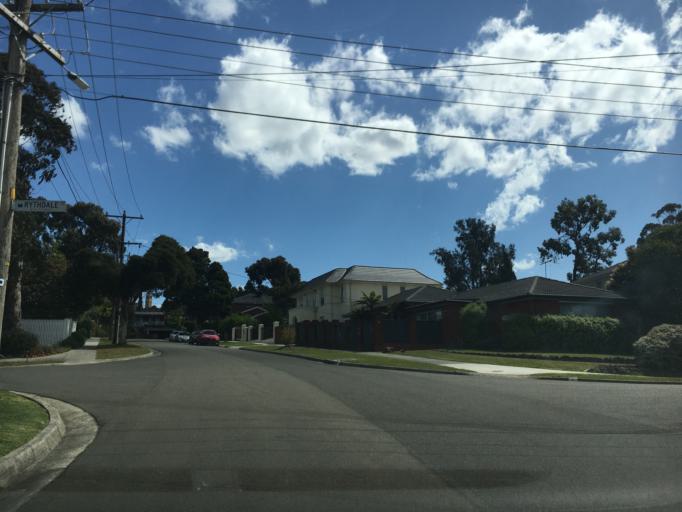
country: AU
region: Victoria
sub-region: Whitehorse
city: Vermont South
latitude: -37.8876
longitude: 145.1837
